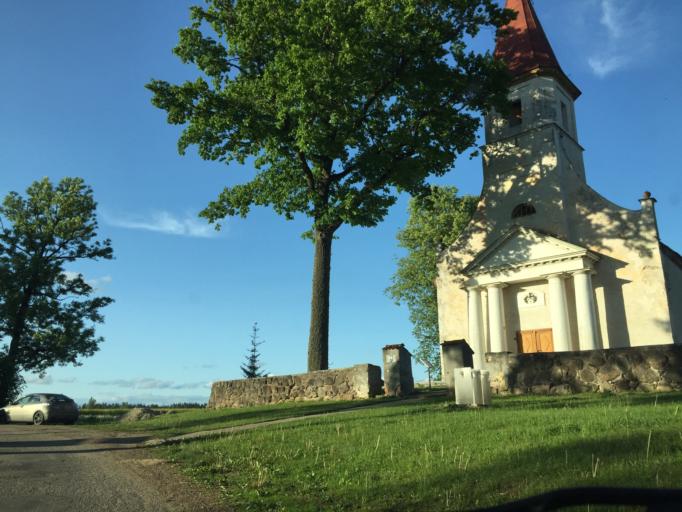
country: LV
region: Koceni
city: Koceni
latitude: 57.4681
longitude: 25.2655
